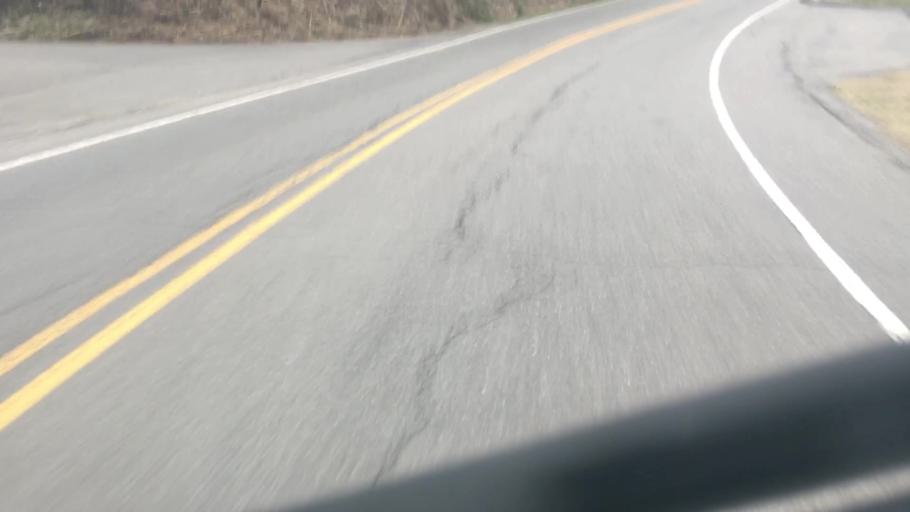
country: US
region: Alabama
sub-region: Jefferson County
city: Hoover
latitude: 33.3647
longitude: -86.8138
